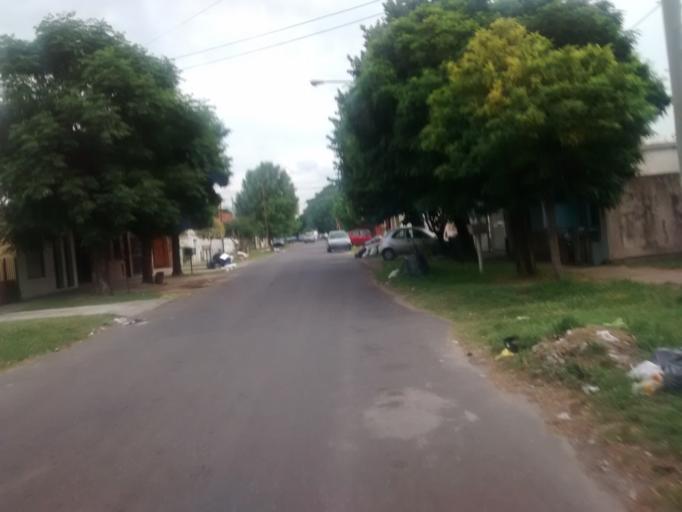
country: AR
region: Buenos Aires
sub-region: Partido de La Plata
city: La Plata
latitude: -34.9416
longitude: -57.9366
